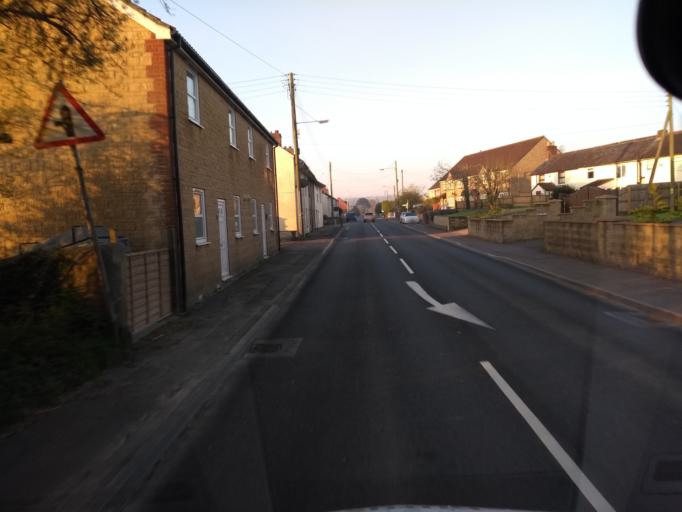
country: GB
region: England
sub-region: Somerset
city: Chard
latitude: 50.8837
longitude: -2.9528
